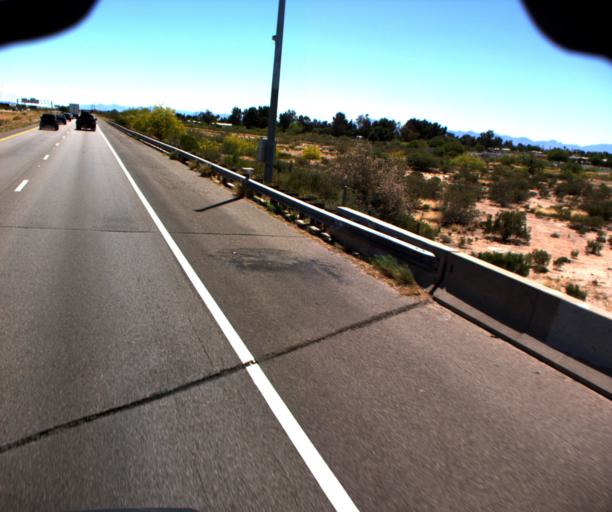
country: US
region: Arizona
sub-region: Pima County
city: Tucson
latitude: 32.1570
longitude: -110.9091
